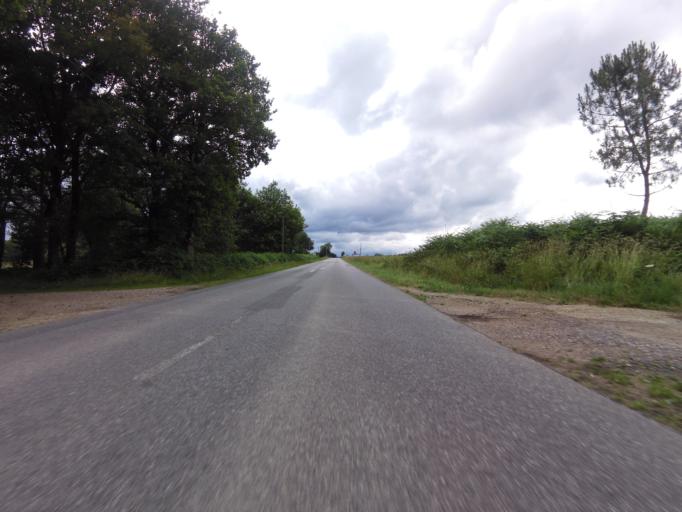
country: FR
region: Brittany
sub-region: Departement du Morbihan
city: Saint-Martin-sur-Oust
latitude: 47.7269
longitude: -2.2921
